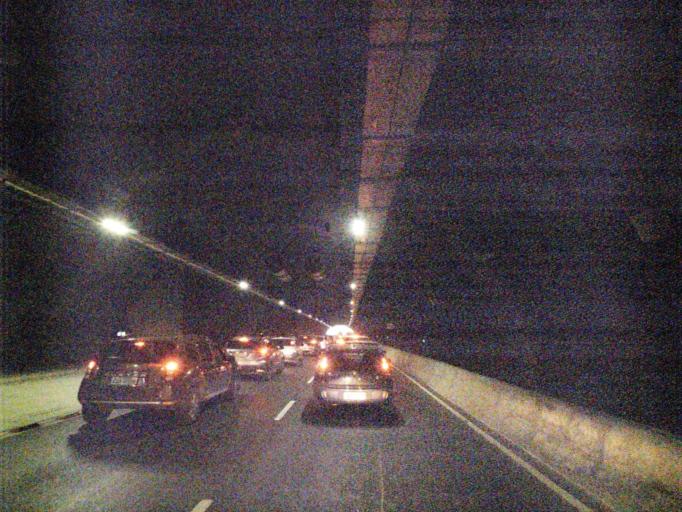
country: BR
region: Rio de Janeiro
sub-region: Niteroi
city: Niteroi
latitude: -22.9341
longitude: -43.0932
